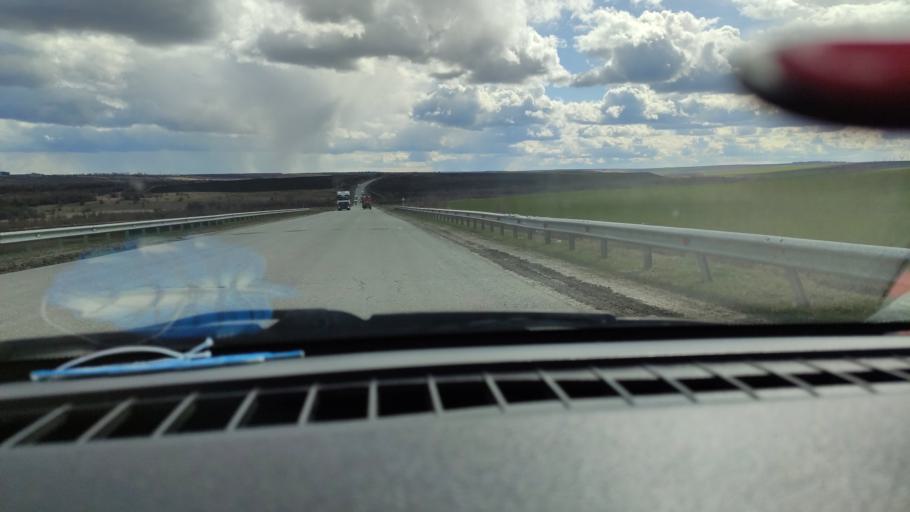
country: RU
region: Samara
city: Varlamovo
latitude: 53.0748
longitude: 48.3542
